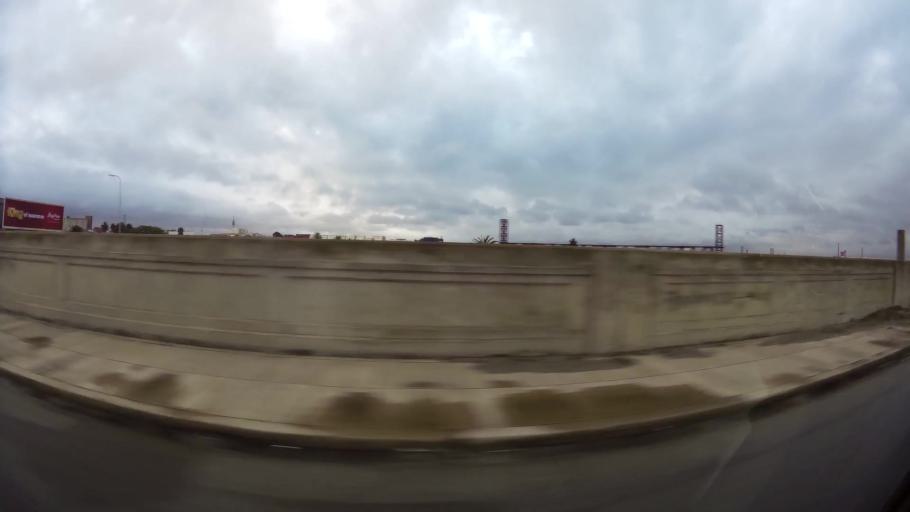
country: ZA
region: Eastern Cape
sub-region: Nelson Mandela Bay Metropolitan Municipality
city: Port Elizabeth
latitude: -33.9253
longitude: 25.6051
